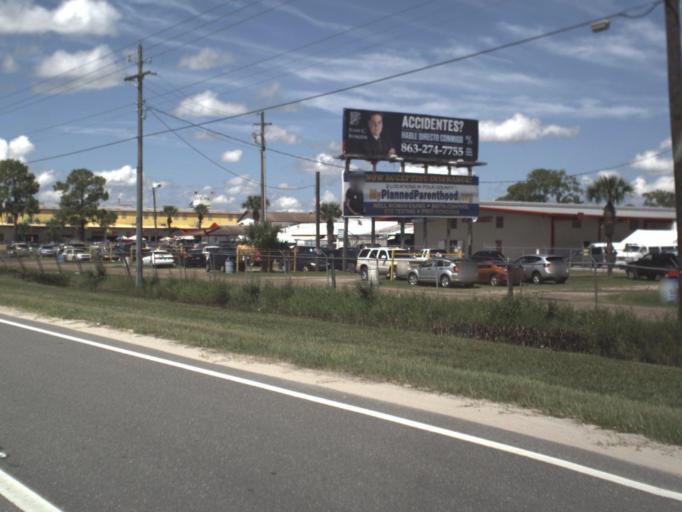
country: US
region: Florida
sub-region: Polk County
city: Fussels Corner
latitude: 28.0561
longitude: -81.8273
